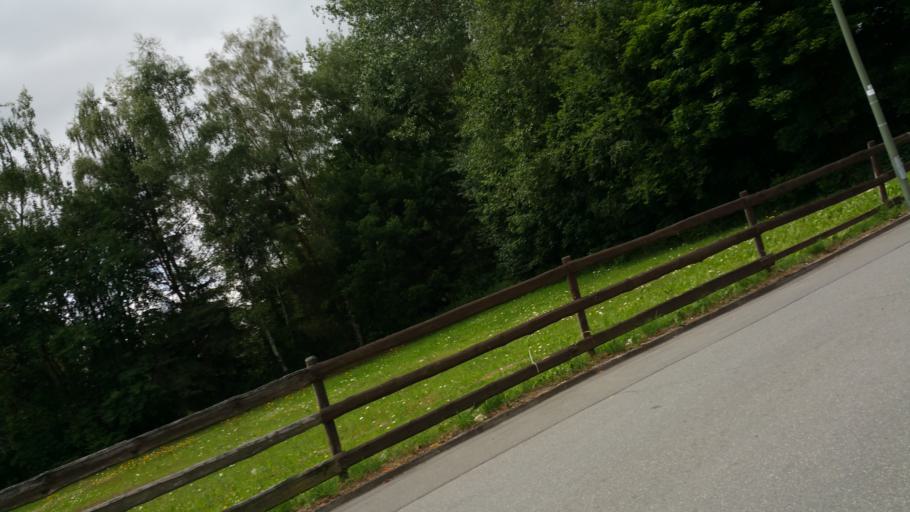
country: DE
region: Bavaria
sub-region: Upper Franconia
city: Rehau
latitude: 50.2391
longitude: 12.0218
